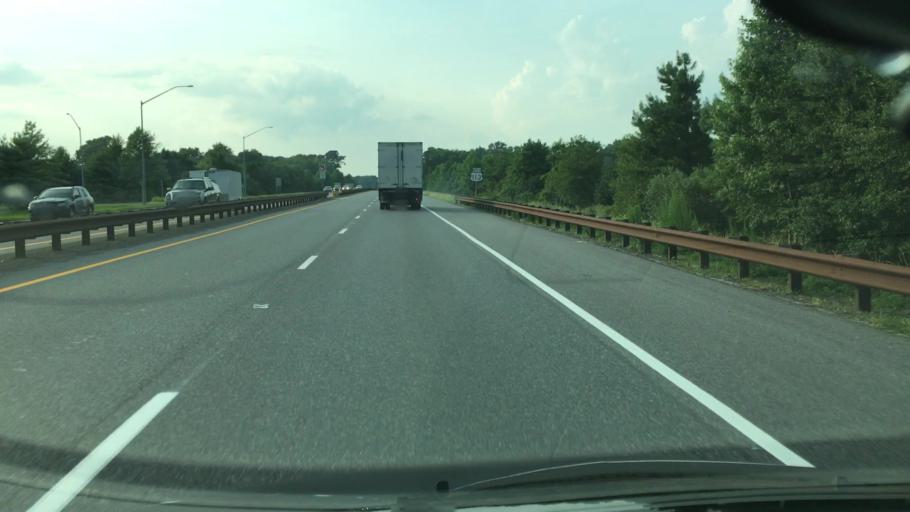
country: US
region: Maryland
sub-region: Worcester County
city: Ocean Pines
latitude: 38.3966
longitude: -75.2060
